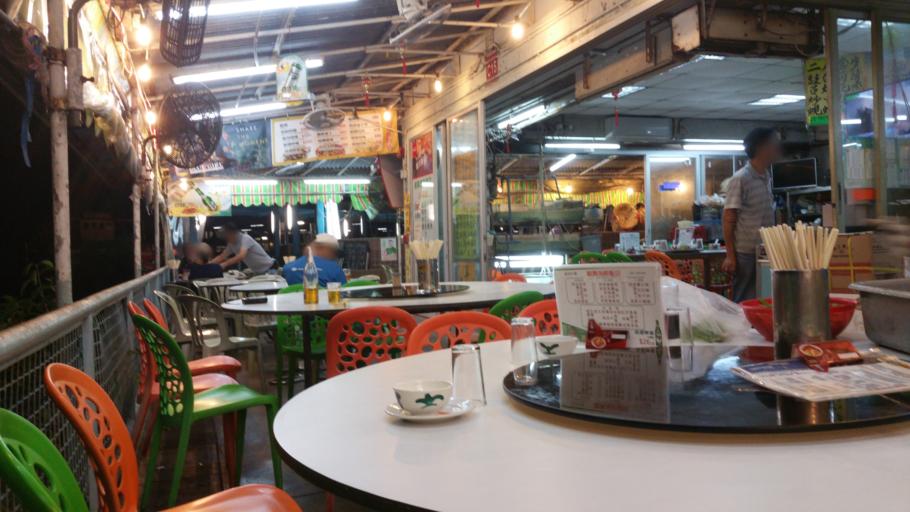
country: HK
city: Yung Shue Wan
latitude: 22.2659
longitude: 114.0012
